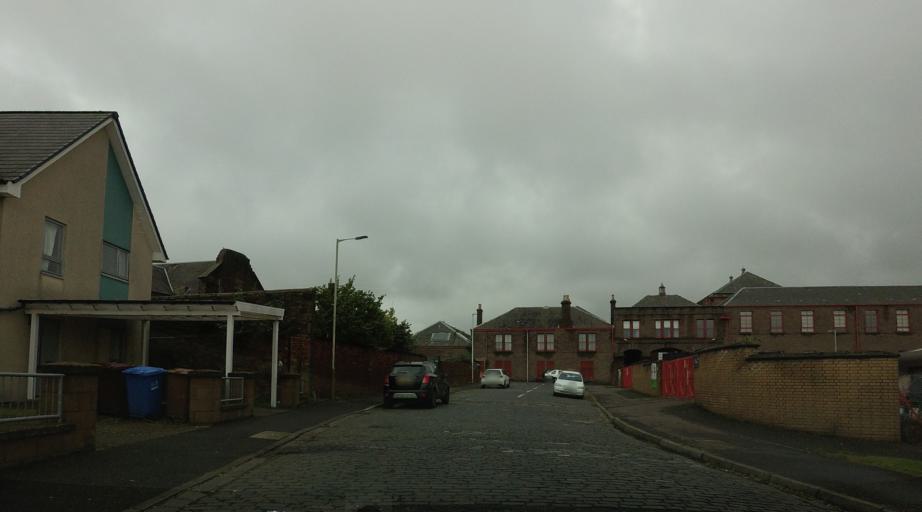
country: GB
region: Scotland
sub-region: Dundee City
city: Dundee
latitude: 56.4699
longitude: -2.9701
